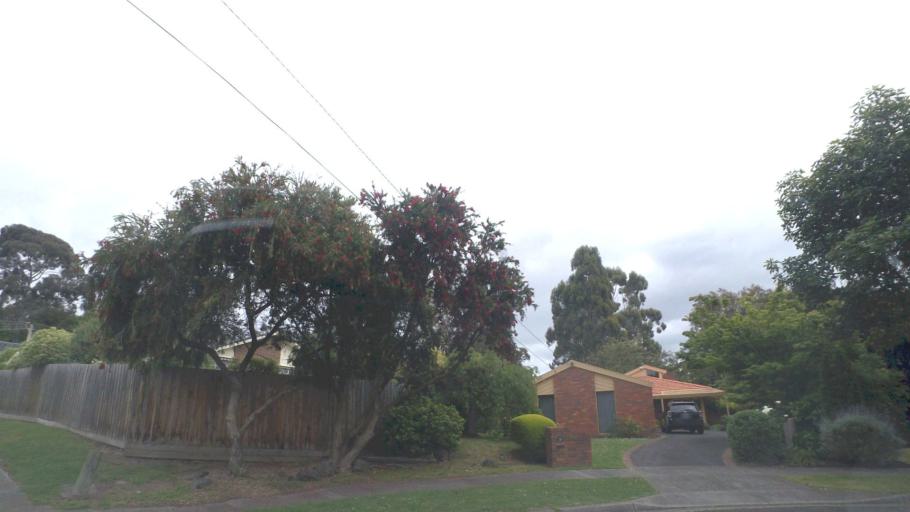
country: AU
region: Victoria
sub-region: Maroondah
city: Croydon South
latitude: -37.8031
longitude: 145.2666
